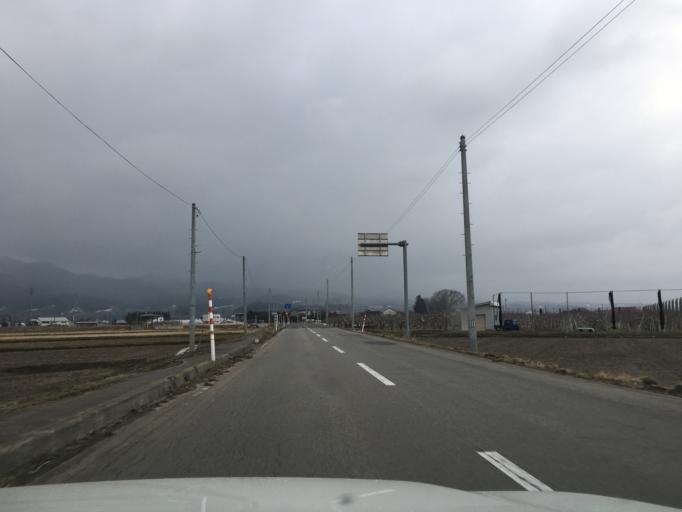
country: JP
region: Aomori
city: Hirosaki
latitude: 40.5609
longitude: 140.5496
